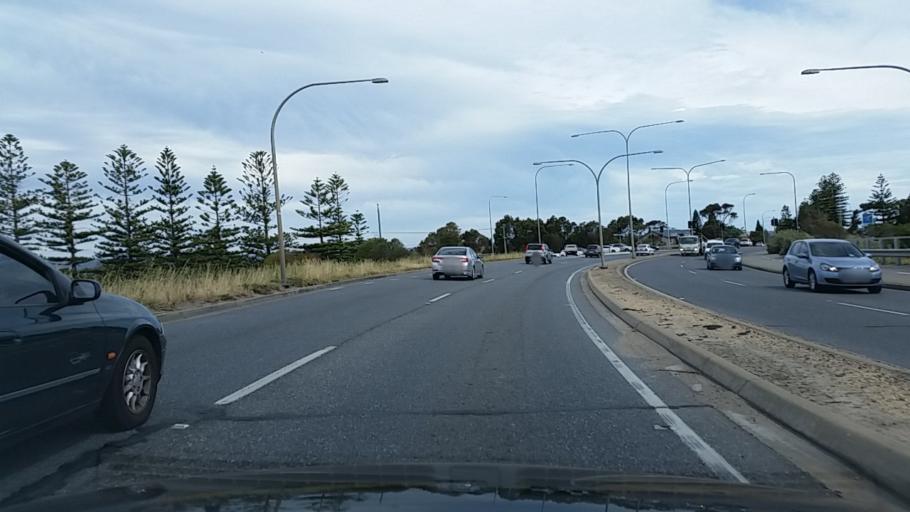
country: AU
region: South Australia
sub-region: Adelaide
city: Glenelg
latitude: -34.9615
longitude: 138.5165
